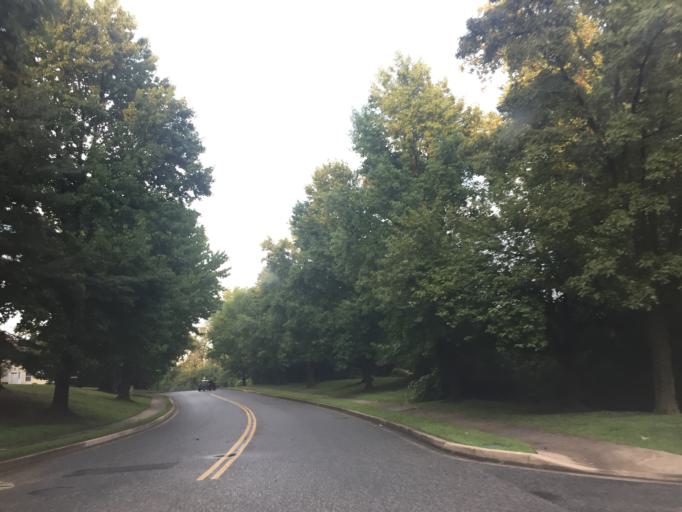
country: US
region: Maryland
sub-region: Harford County
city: Riverside
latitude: 39.4721
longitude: -76.2428
